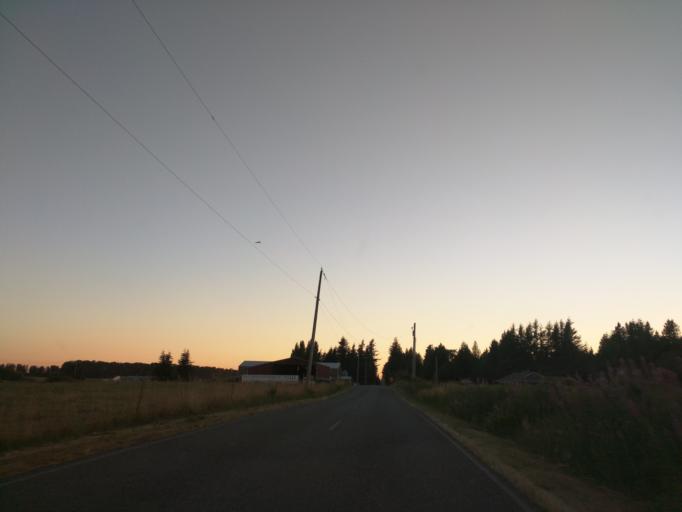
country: US
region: Washington
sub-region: Whatcom County
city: Everson
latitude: 48.9346
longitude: -122.3708
